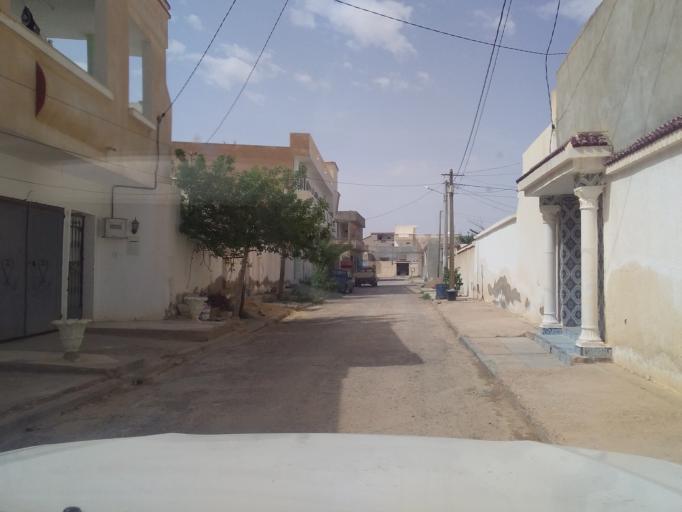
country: TN
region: Qabis
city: Matmata
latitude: 33.6156
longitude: 10.2794
